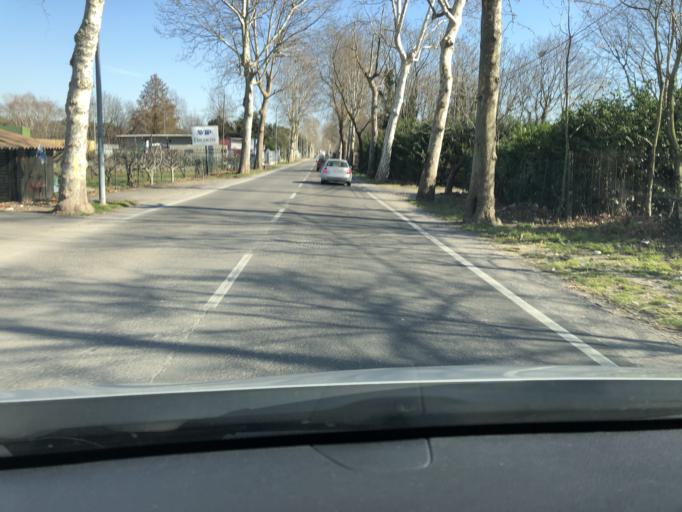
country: IT
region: Veneto
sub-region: Provincia di Verona
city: Bassone
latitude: 45.4466
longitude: 10.9074
